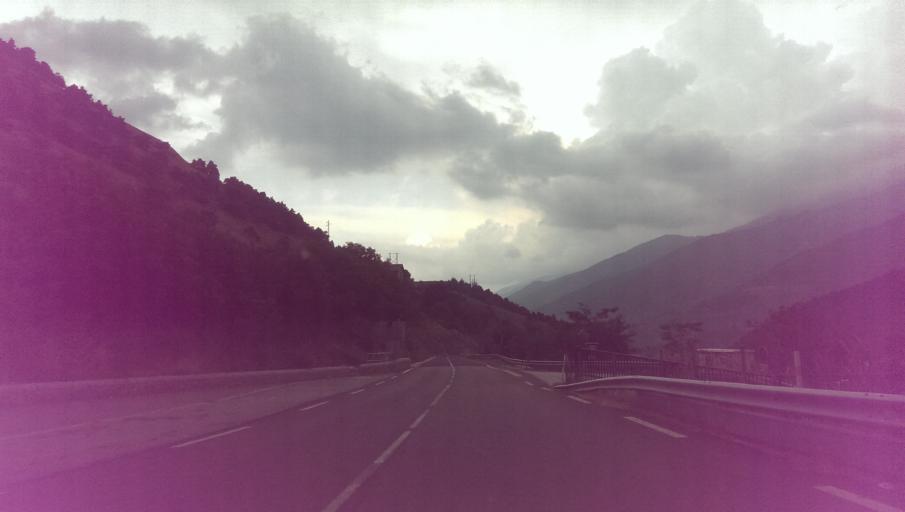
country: ES
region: Catalonia
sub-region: Provincia de Girona
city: Llivia
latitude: 42.5060
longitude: 2.1516
